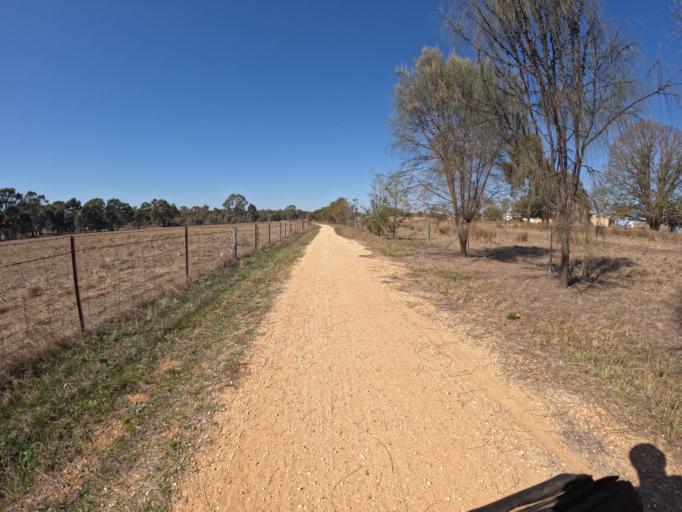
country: AU
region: Victoria
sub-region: Greater Bendigo
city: Kennington
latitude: -36.8281
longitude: 144.5875
